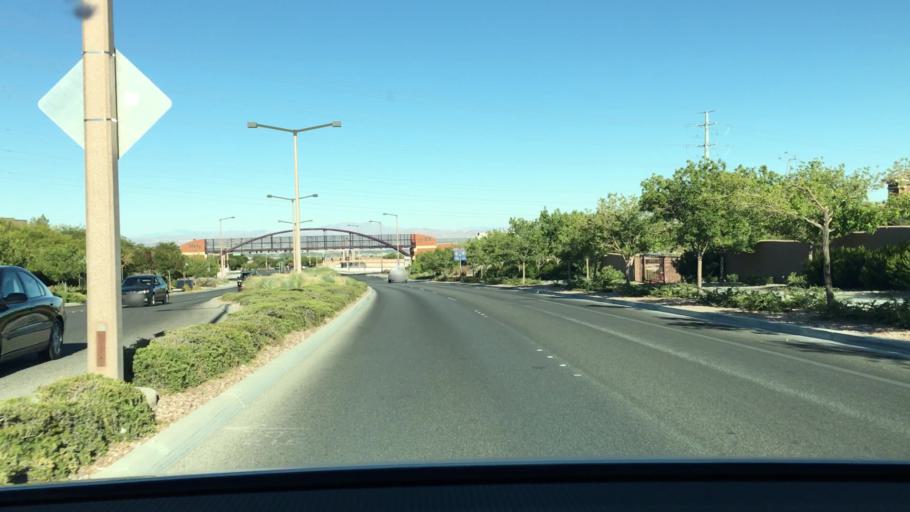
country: US
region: Nevada
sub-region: Clark County
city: Summerlin South
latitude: 36.1807
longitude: -115.3447
